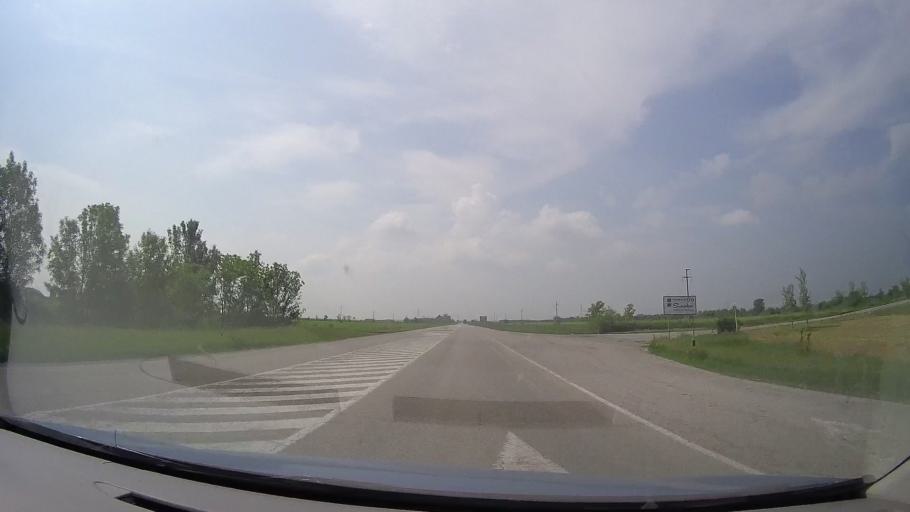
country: RS
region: Autonomna Pokrajina Vojvodina
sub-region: Juznobanatski Okrug
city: Kovacica
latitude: 45.0774
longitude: 20.6410
